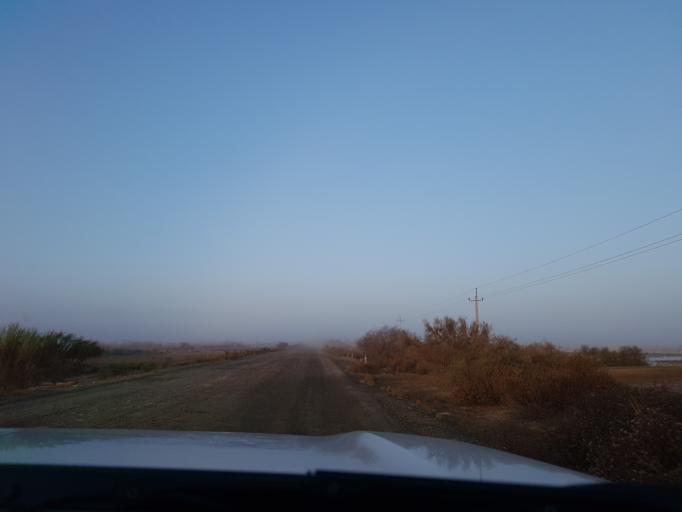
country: TM
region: Dasoguz
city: Koeneuergench
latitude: 41.8446
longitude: 58.5630
